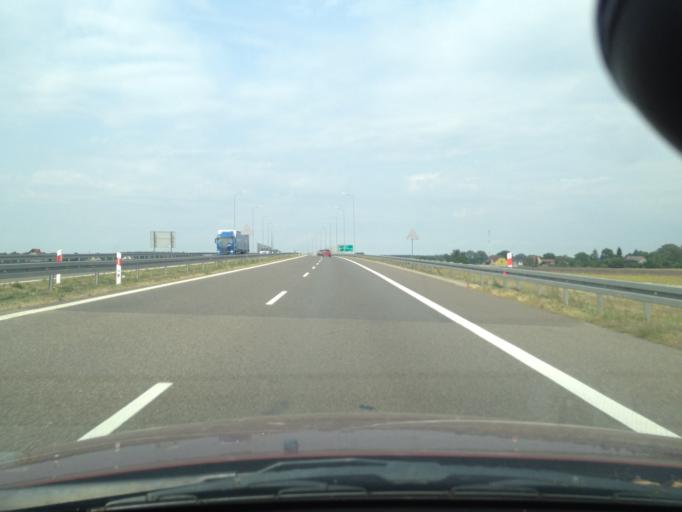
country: PL
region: West Pomeranian Voivodeship
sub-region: Powiat pyrzycki
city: Lipiany
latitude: 52.9471
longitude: 14.9633
